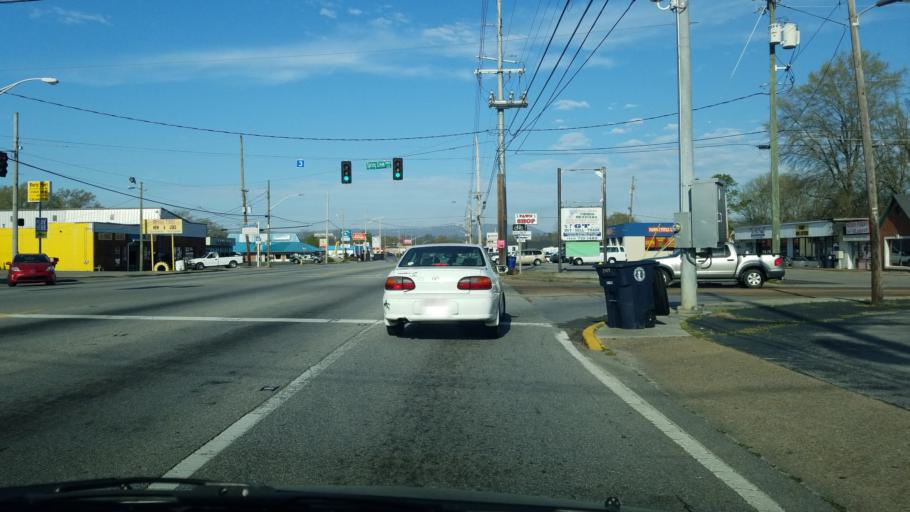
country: US
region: Tennessee
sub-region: Hamilton County
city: East Ridge
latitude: 34.9901
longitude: -85.2152
